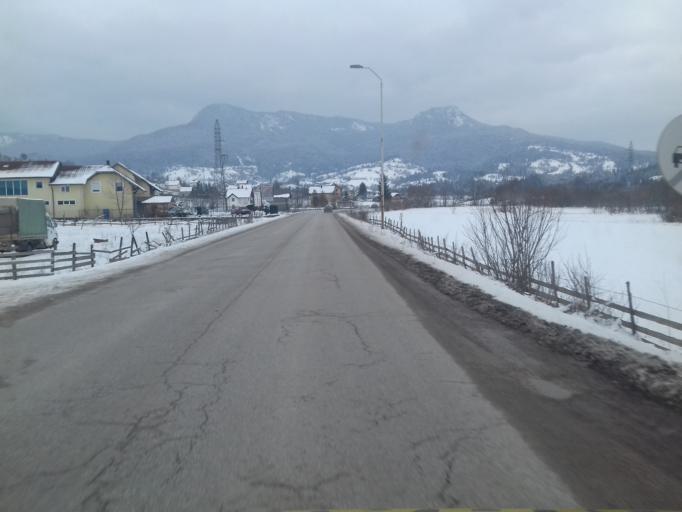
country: BA
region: Republika Srpska
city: Pale
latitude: 43.8736
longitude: 18.5806
